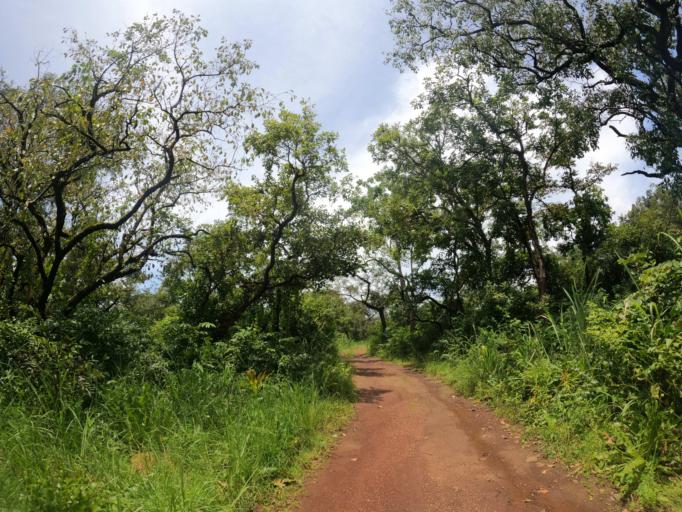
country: SL
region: Northern Province
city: Binkolo
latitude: 9.1576
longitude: -12.2020
